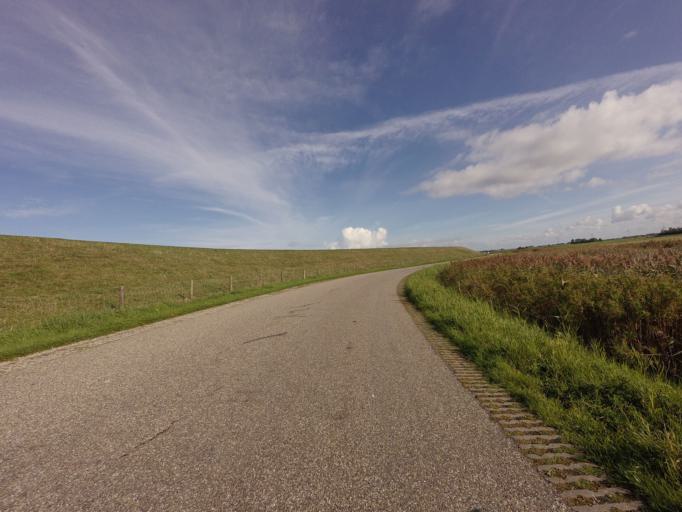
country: NL
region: Friesland
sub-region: Sudwest Fryslan
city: Makkum
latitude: 53.0695
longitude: 5.3906
